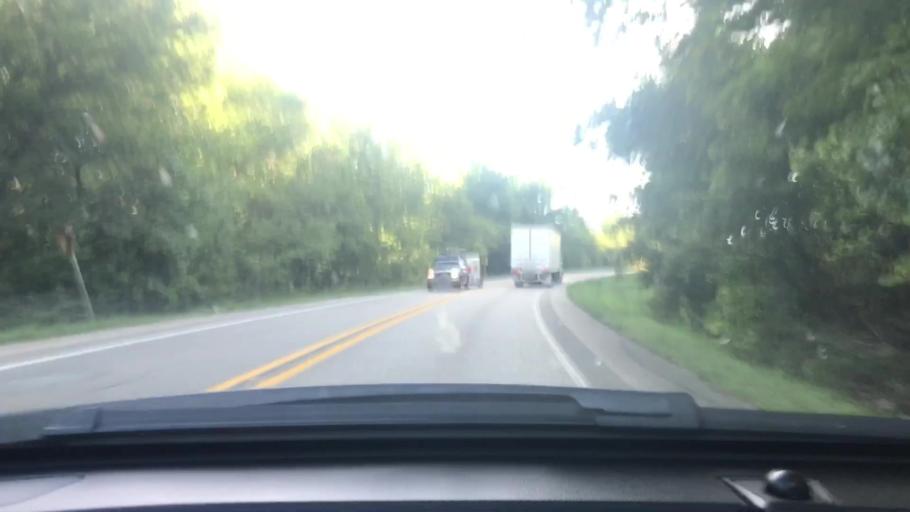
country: US
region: Arkansas
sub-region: Randolph County
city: Pocahontas
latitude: 36.2163
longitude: -91.2159
